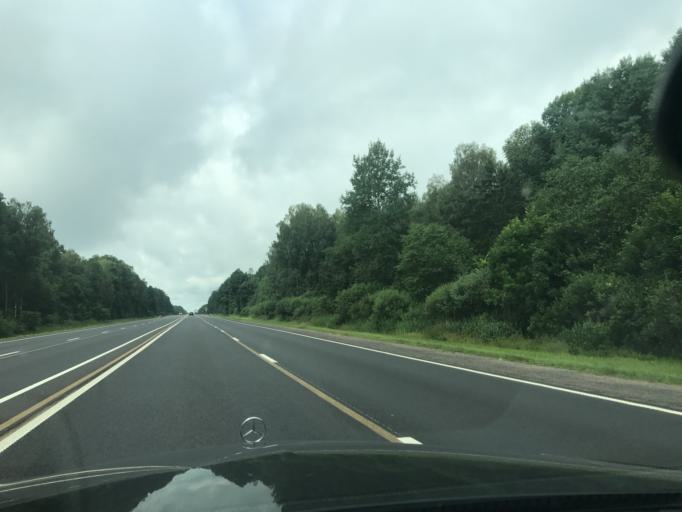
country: RU
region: Smolensk
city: Katyn'
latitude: 54.7783
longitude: 31.5510
